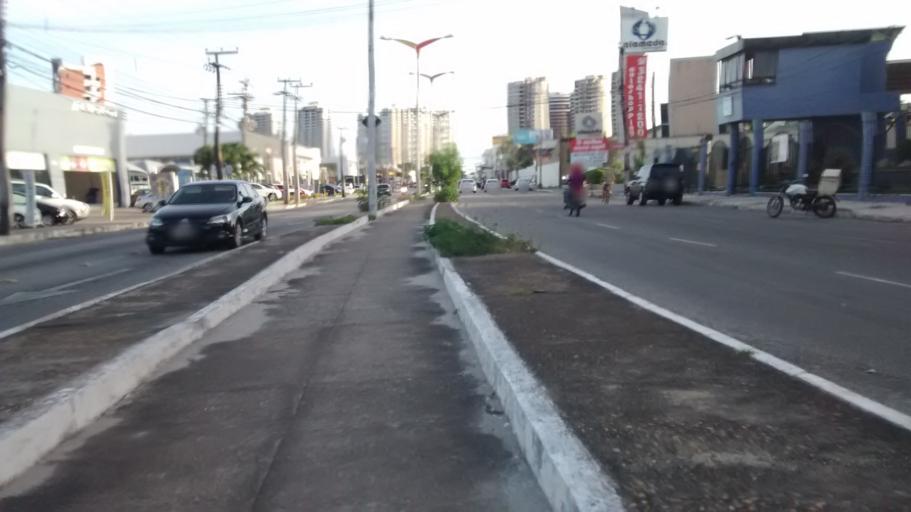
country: BR
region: Ceara
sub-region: Fortaleza
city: Fortaleza
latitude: -3.7597
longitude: -38.4922
